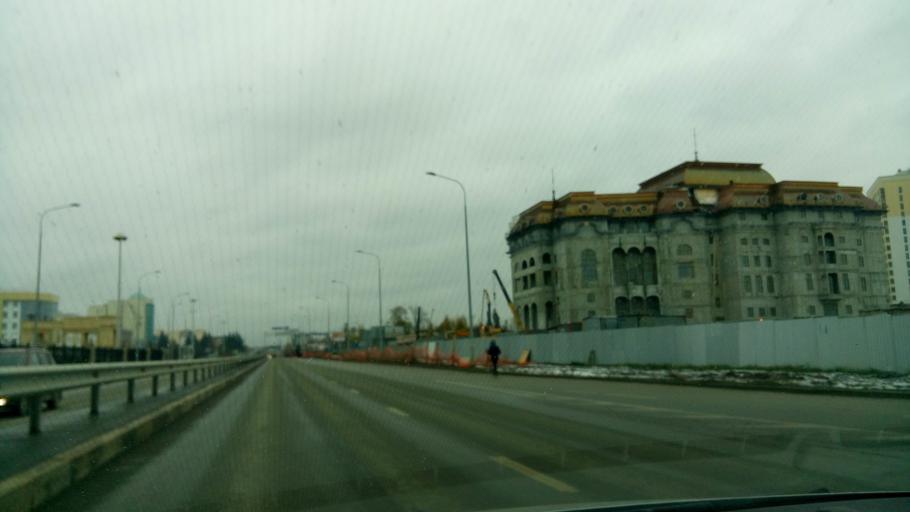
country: RU
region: Sverdlovsk
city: Verkhnyaya Pyshma
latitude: 56.9636
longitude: 60.5828
